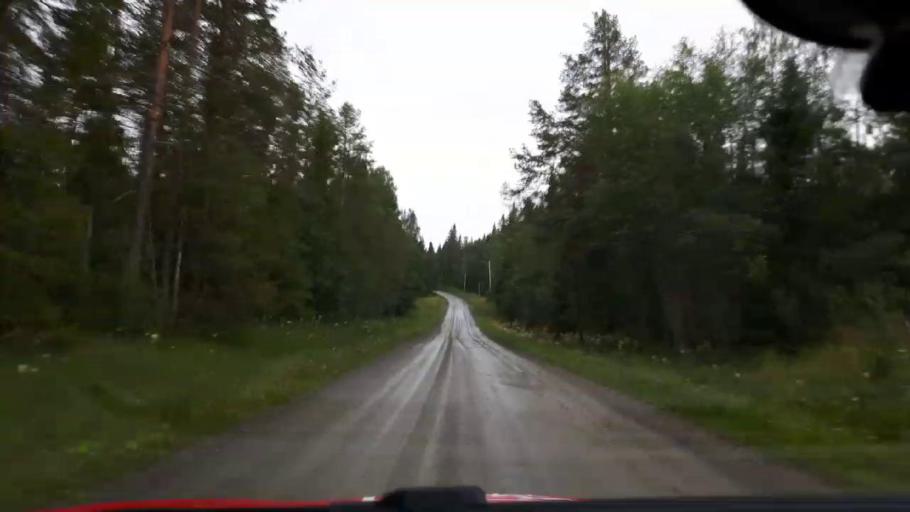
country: SE
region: Jaemtland
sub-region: OEstersunds Kommun
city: Brunflo
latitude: 62.9027
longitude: 14.8593
